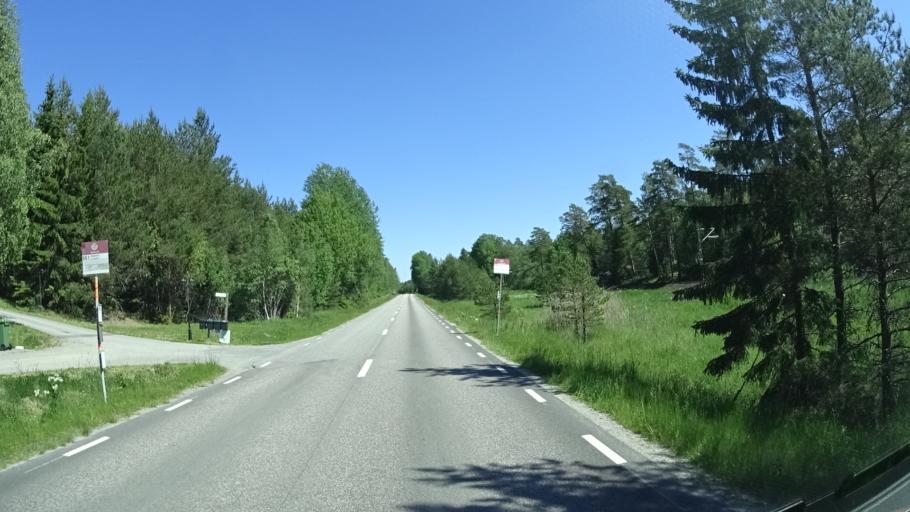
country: SE
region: Stockholm
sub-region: Vallentuna Kommun
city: Vallentuna
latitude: 59.6078
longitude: 18.1470
